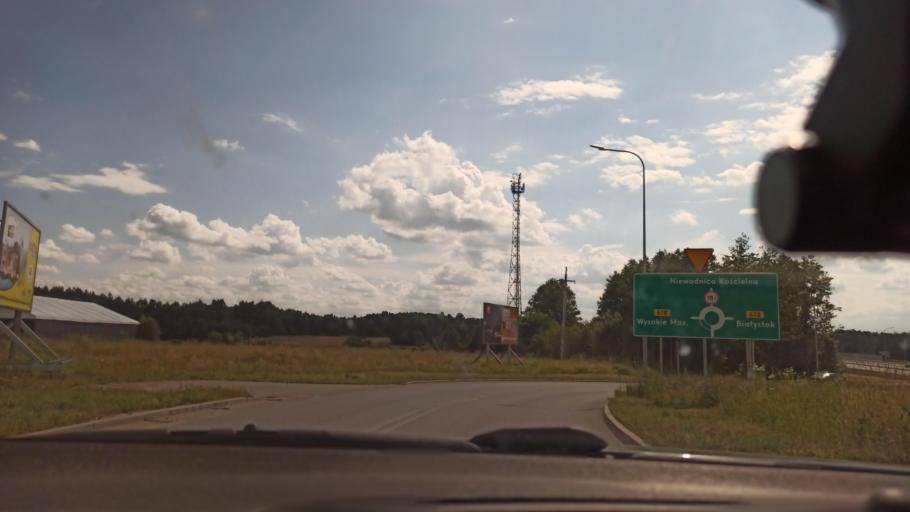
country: PL
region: Podlasie
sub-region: Powiat bialostocki
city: Turosn Koscielna
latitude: 53.0688
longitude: 23.0803
